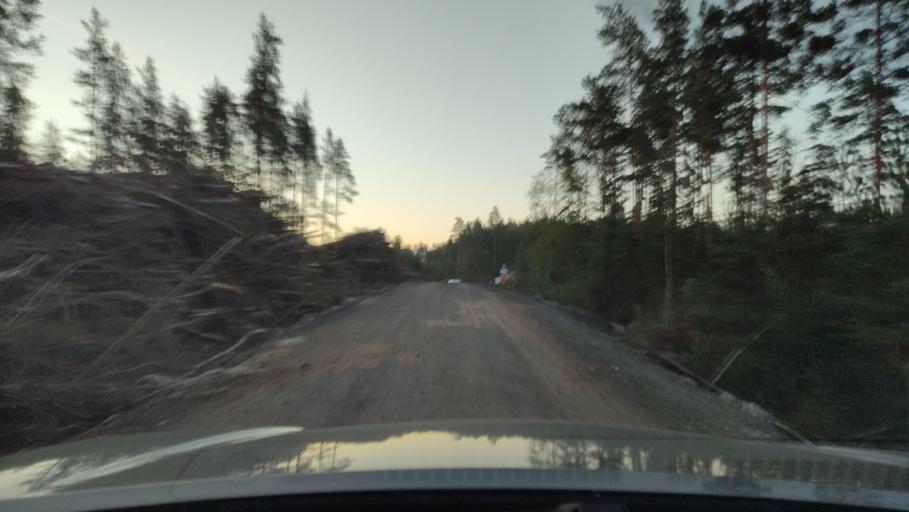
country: FI
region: Ostrobothnia
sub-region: Sydosterbotten
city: Kristinestad
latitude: 62.1918
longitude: 21.5203
